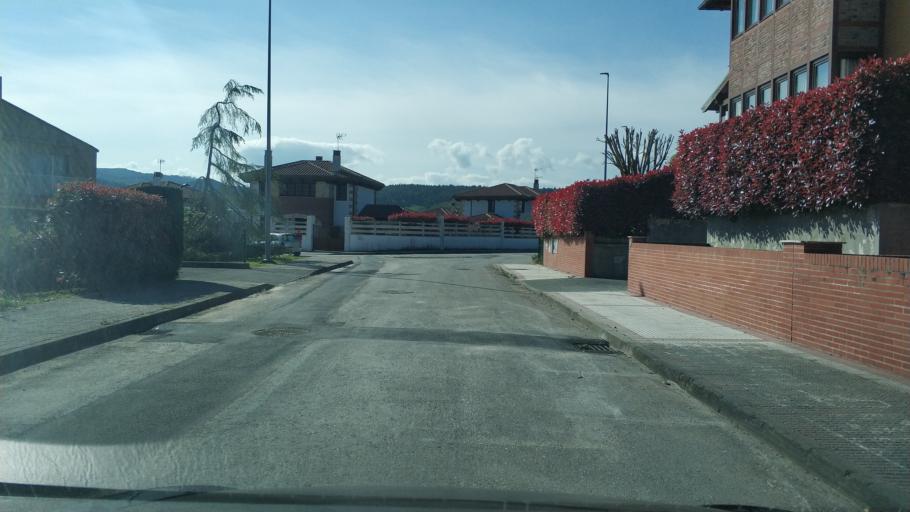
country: ES
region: Cantabria
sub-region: Provincia de Cantabria
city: Comillas
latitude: 43.3801
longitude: -4.2823
